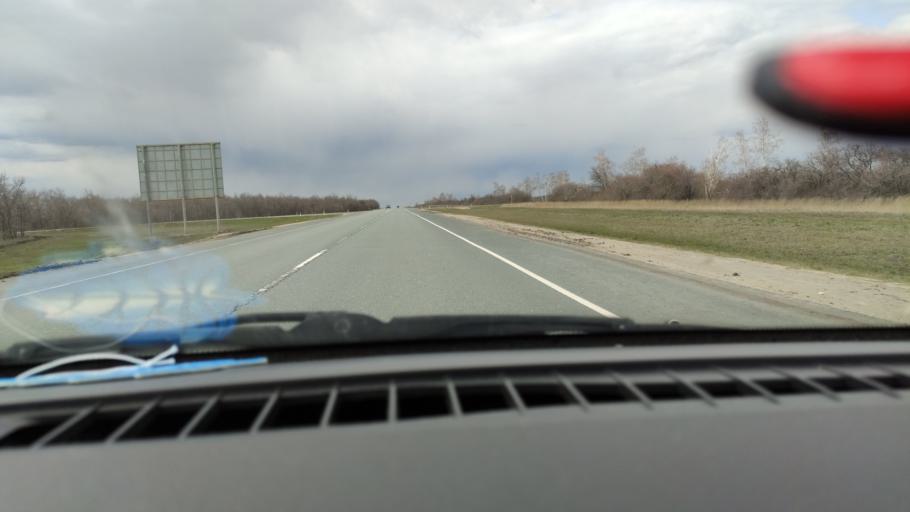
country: RU
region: Saratov
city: Yelshanka
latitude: 51.8210
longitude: 46.3398
